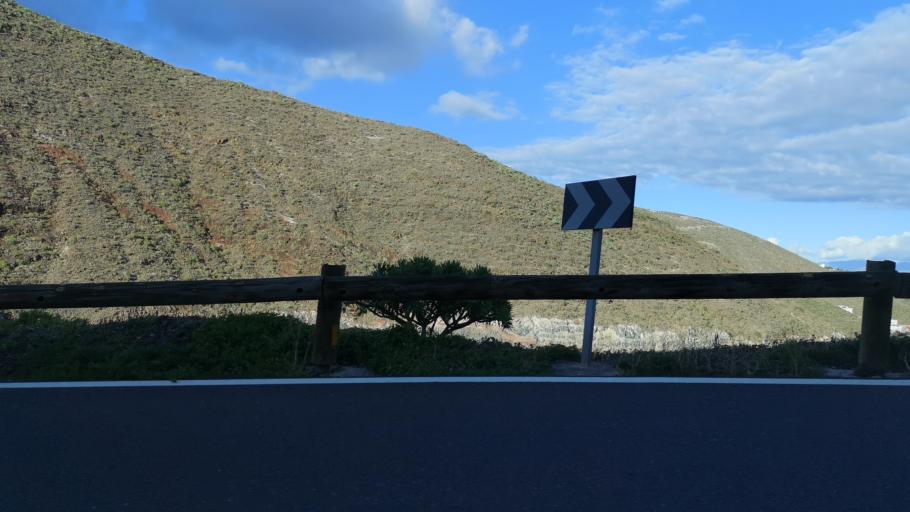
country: ES
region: Canary Islands
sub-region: Provincia de Santa Cruz de Tenerife
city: San Sebastian de la Gomera
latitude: 28.0857
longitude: -17.1276
